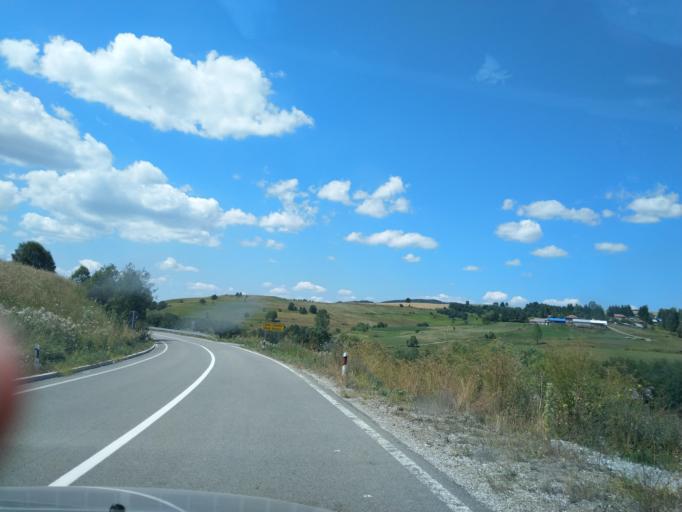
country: RS
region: Central Serbia
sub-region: Zlatiborski Okrug
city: Sjenica
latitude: 43.3275
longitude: 19.8931
